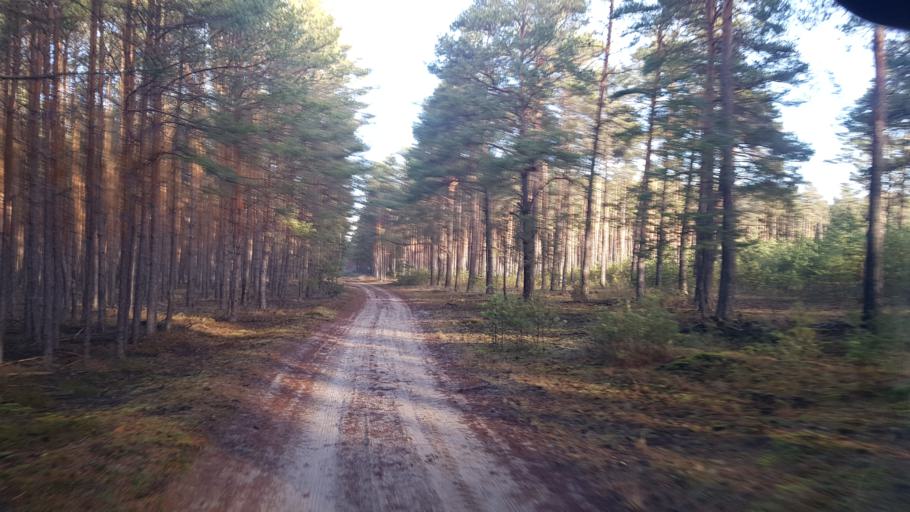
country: DE
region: Brandenburg
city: Schilda
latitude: 51.6272
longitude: 13.3933
